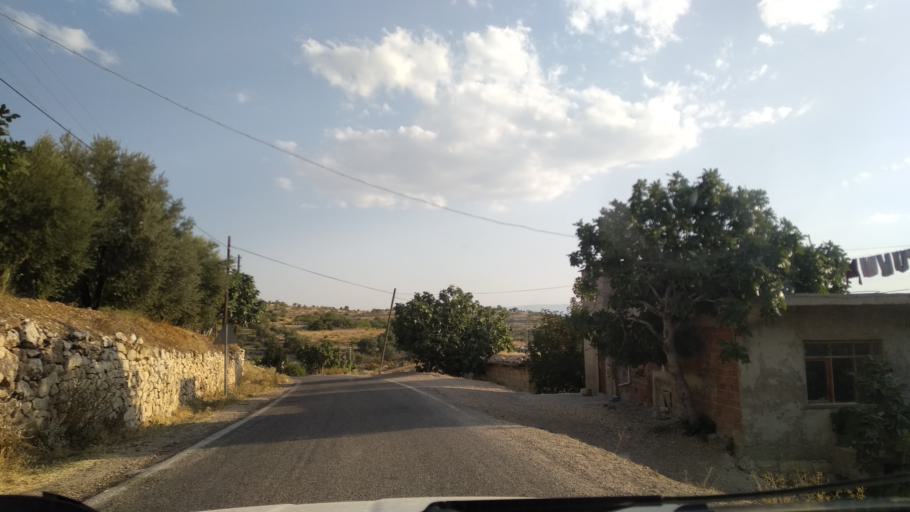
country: TR
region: Mersin
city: Sarikavak
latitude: 36.5783
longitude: 33.6437
